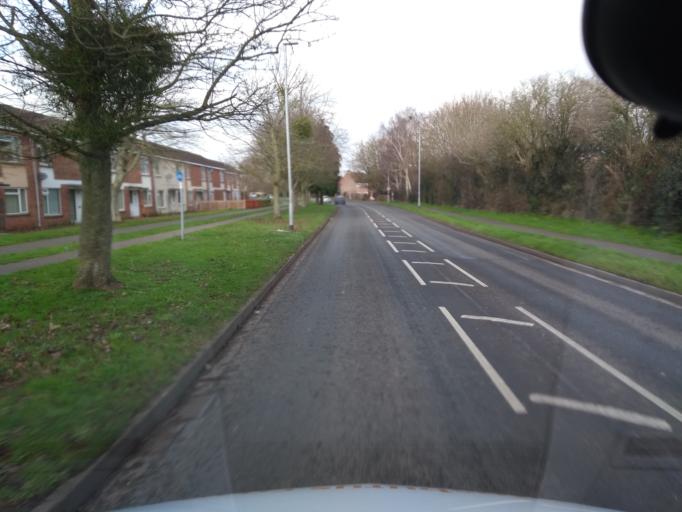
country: GB
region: England
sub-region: Somerset
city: Taunton
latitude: 51.0113
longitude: -3.0757
